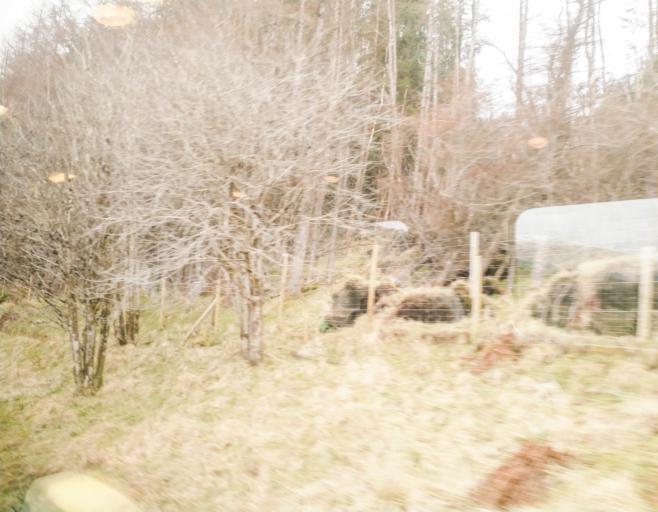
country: GB
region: Scotland
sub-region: Argyll and Bute
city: Garelochhead
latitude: 56.4404
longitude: -4.7072
